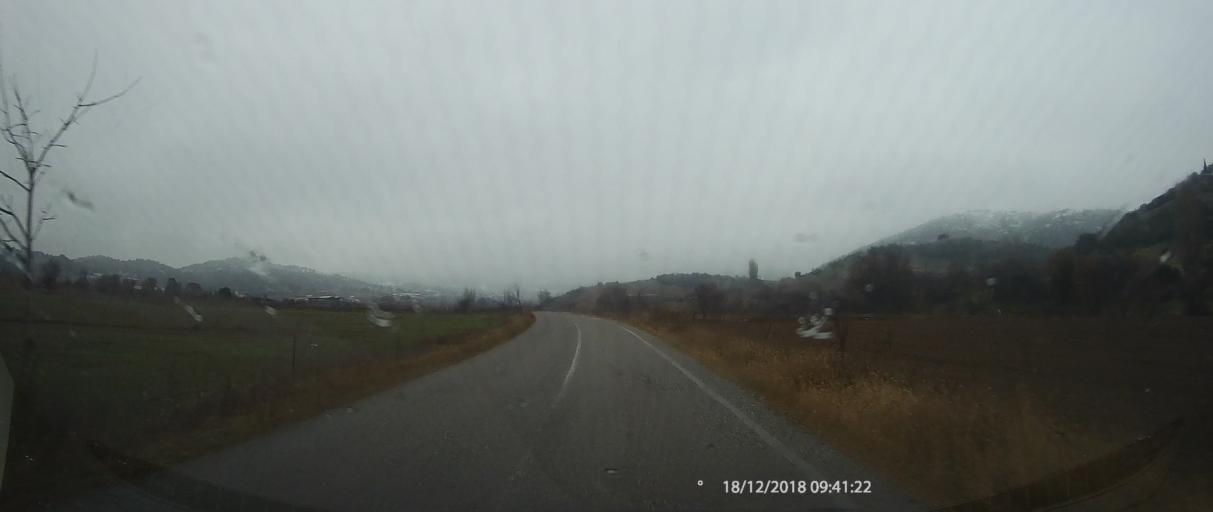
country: GR
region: Thessaly
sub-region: Nomos Larisis
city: Elassona
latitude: 40.0111
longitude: 22.2320
